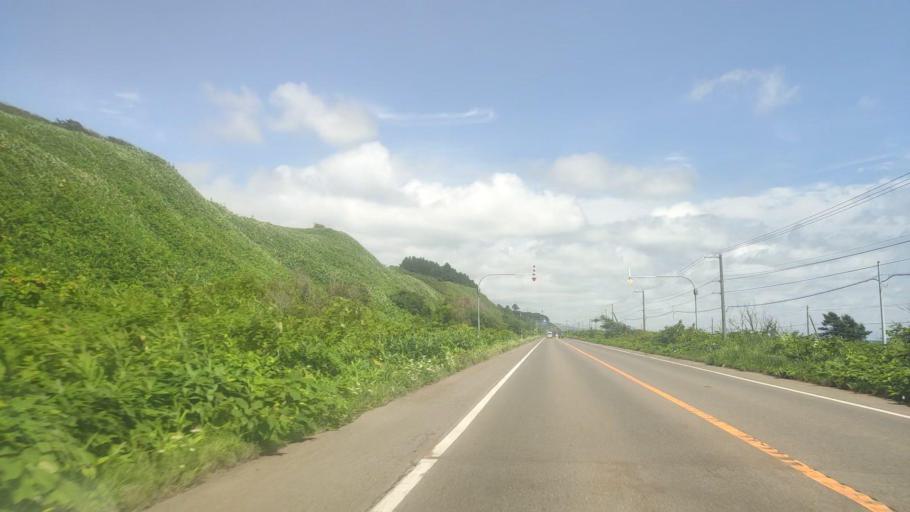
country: JP
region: Hokkaido
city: Niseko Town
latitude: 42.3465
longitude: 140.2824
